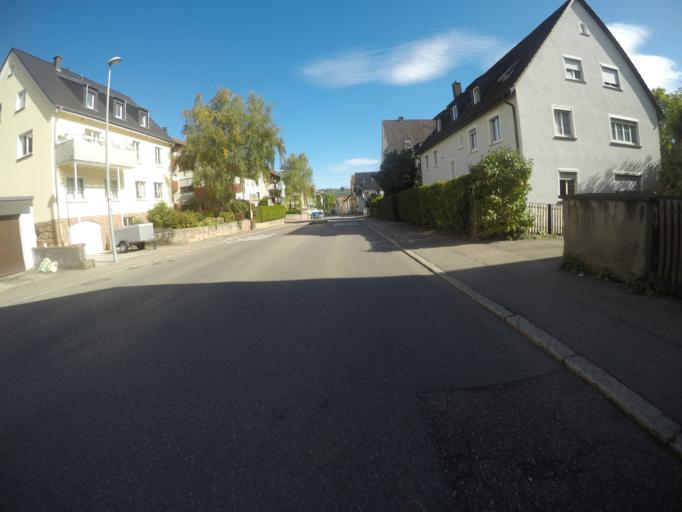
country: DE
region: Baden-Wuerttemberg
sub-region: Regierungsbezirk Stuttgart
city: Ostfildern
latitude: 48.7574
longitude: 9.2463
